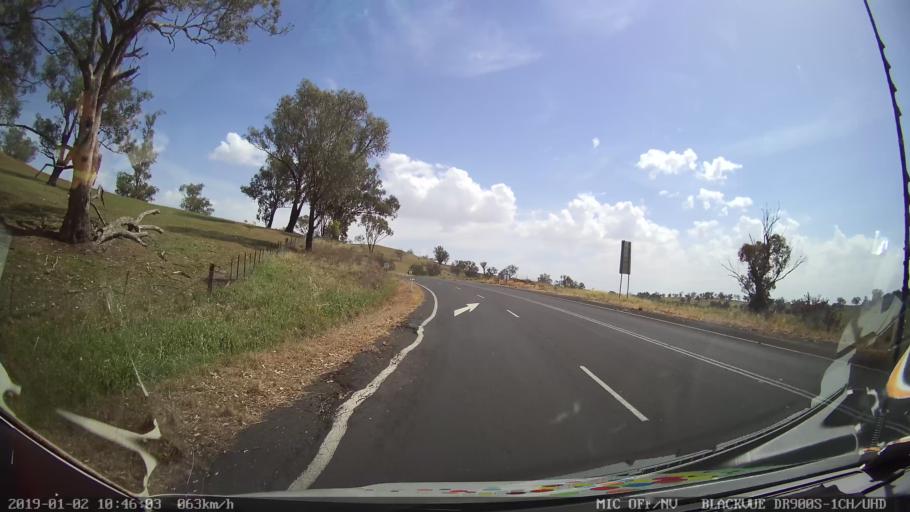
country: AU
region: New South Wales
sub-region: Cootamundra
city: Cootamundra
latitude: -34.7546
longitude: 148.2894
